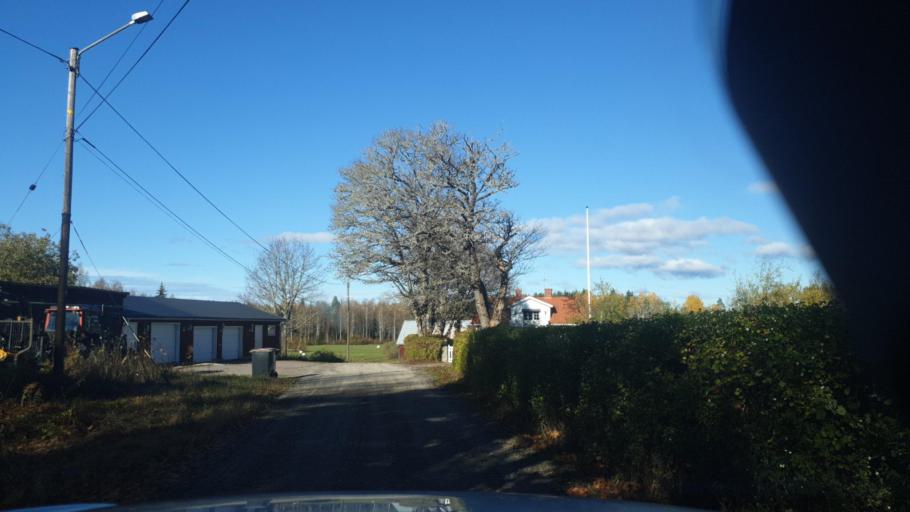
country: SE
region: Vaermland
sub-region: Arvika Kommun
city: Arvika
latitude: 59.5512
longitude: 12.8501
